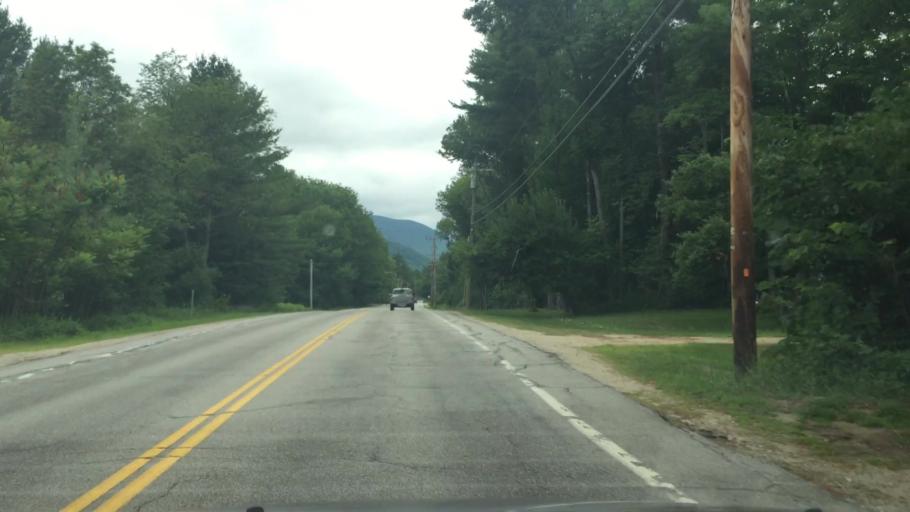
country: US
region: New Hampshire
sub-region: Carroll County
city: North Conway
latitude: 44.0789
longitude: -71.2647
